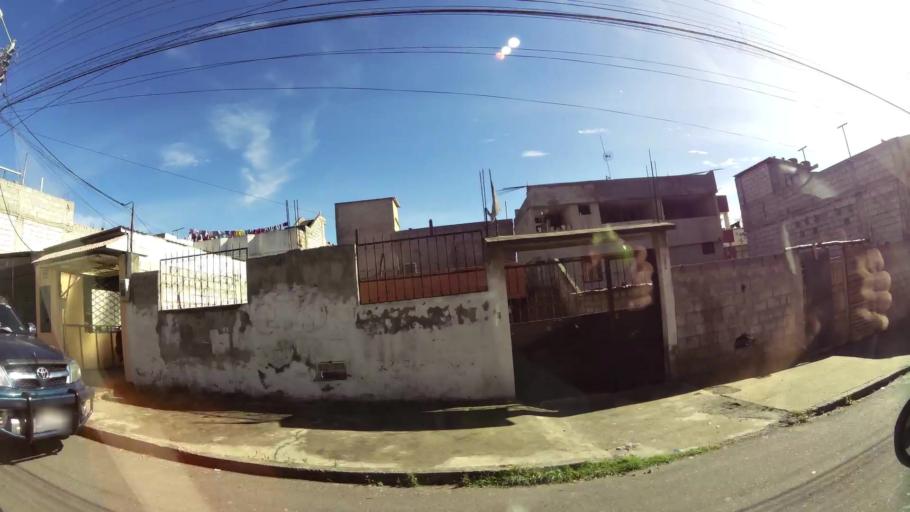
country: EC
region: Pichincha
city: Quito
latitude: -0.3054
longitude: -78.5674
